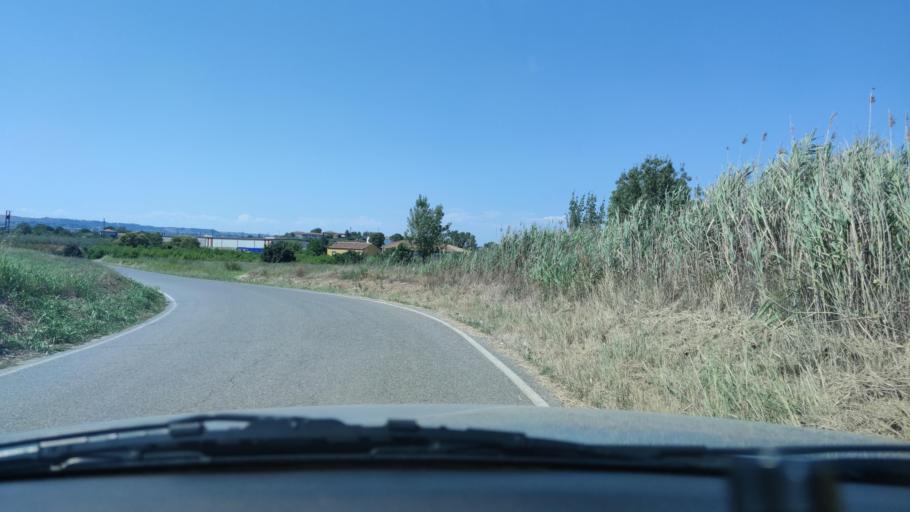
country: ES
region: Catalonia
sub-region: Provincia de Lleida
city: Lleida
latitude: 41.6434
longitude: 0.6237
